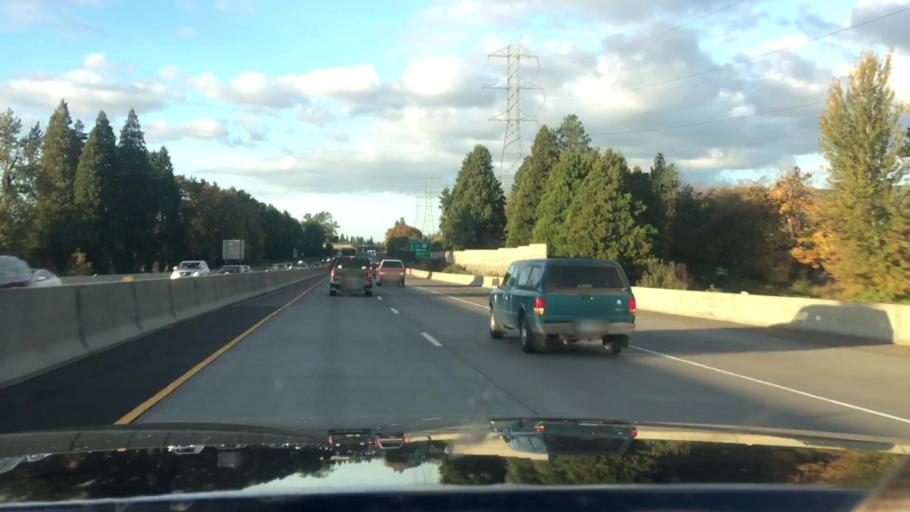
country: US
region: Oregon
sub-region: Lane County
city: Springfield
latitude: 44.0497
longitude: -123.0501
